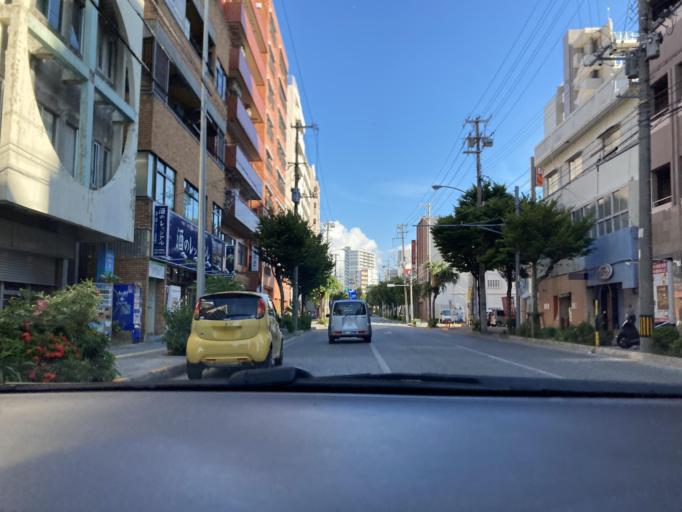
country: JP
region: Okinawa
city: Naha-shi
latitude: 26.2218
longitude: 127.6882
